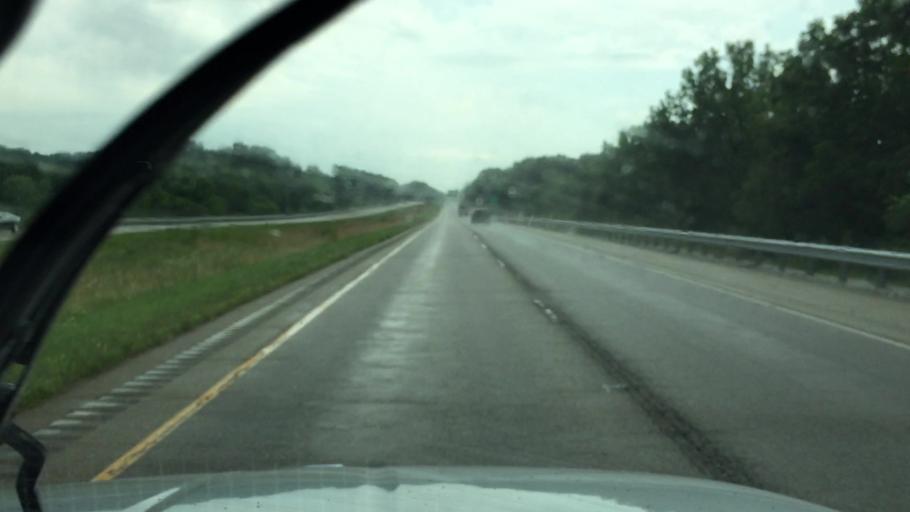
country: US
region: Illinois
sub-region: Peoria County
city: Bellevue
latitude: 40.7502
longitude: -89.6932
